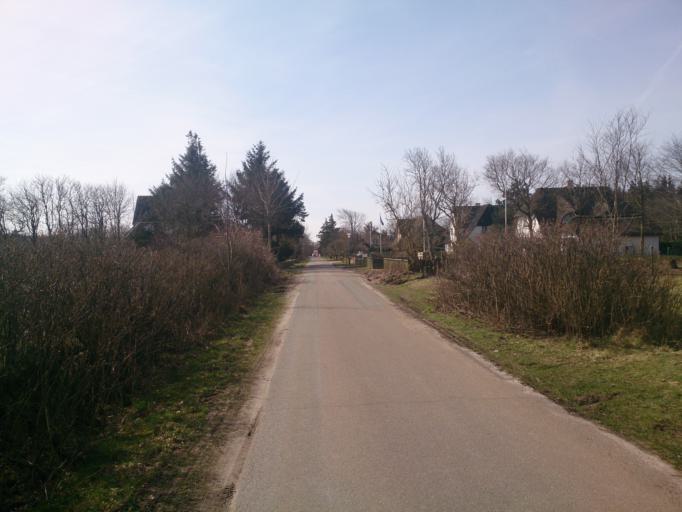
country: DE
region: Schleswig-Holstein
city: Utersum
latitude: 54.7117
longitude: 8.3987
